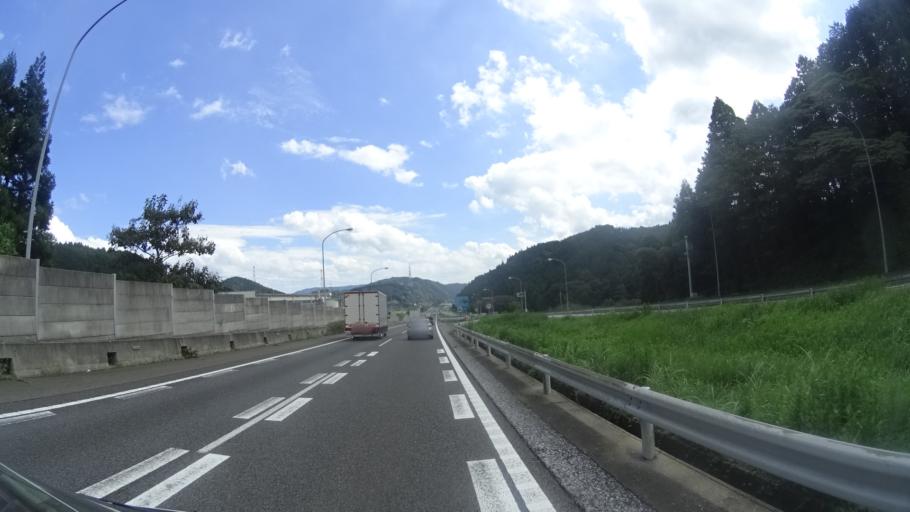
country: JP
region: Gifu
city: Tarui
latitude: 35.3467
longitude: 136.4231
